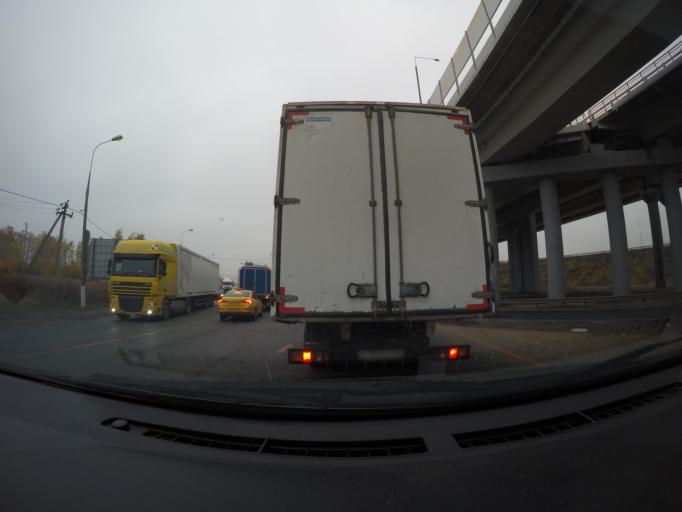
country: RU
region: Moskovskaya
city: Belyye Stolby
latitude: 55.3388
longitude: 37.8040
